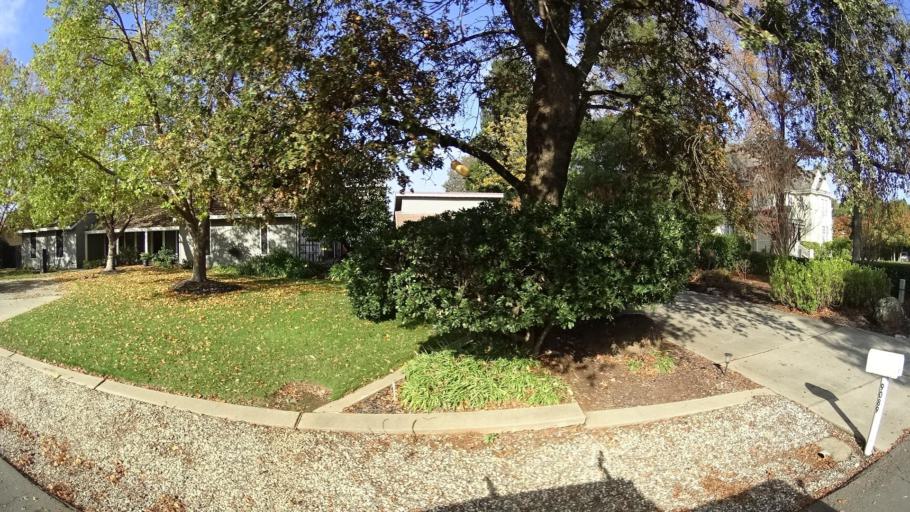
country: US
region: California
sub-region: Sacramento County
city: Elk Grove
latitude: 38.4145
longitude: -121.3625
